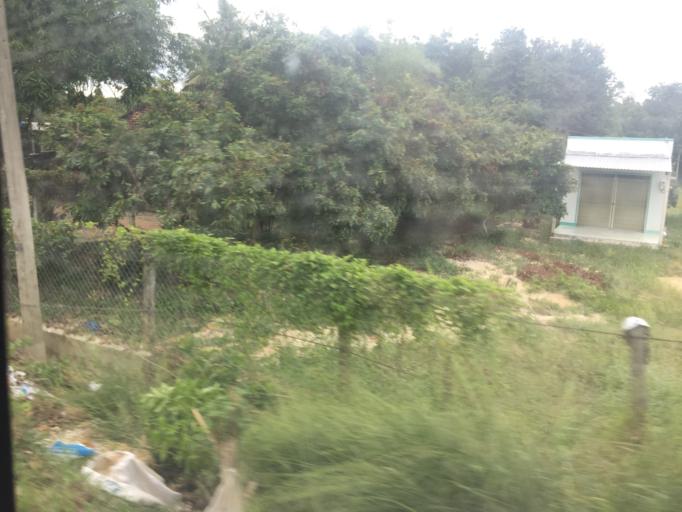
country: VN
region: Ho Chi Minh City
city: Cu Chi
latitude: 11.1235
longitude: 106.4796
